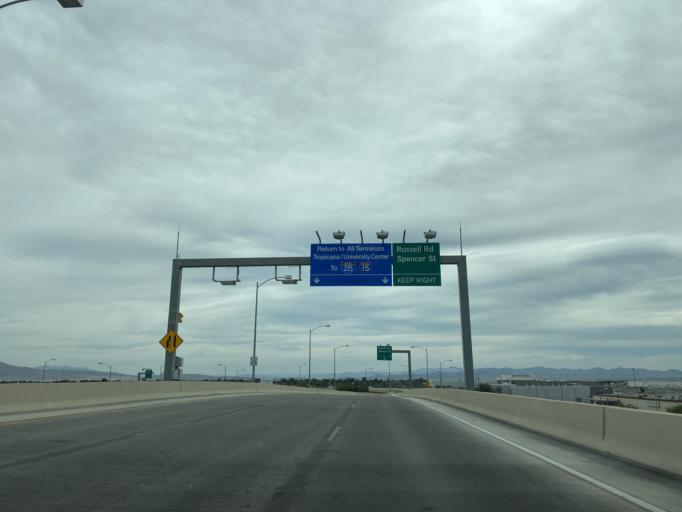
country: US
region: Nevada
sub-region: Clark County
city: Paradise
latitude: 36.0868
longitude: -115.1341
